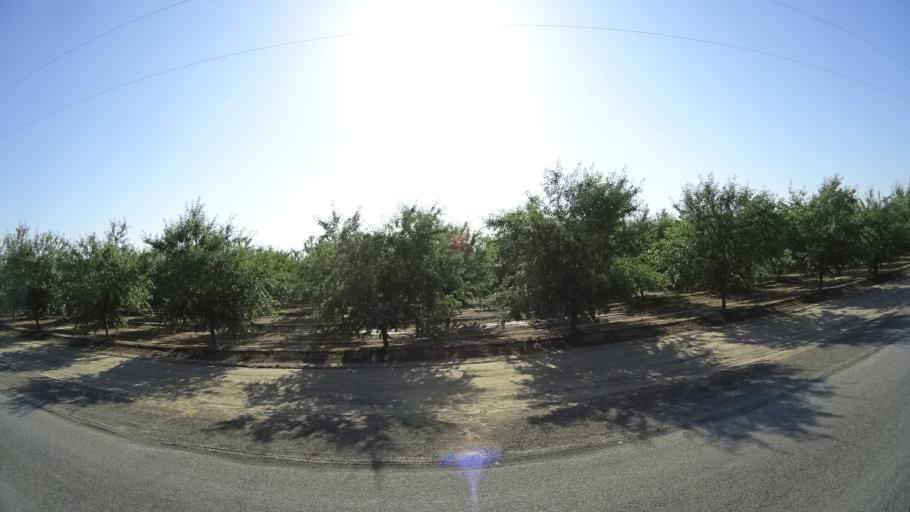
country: US
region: California
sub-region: Kings County
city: Home Garden
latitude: 36.2716
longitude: -119.5652
